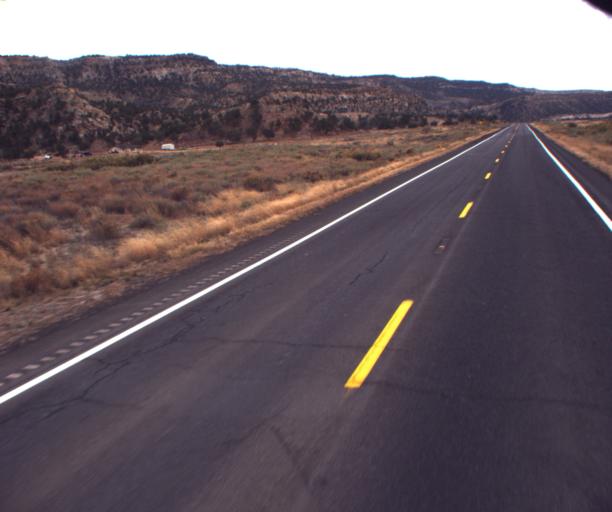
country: US
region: Arizona
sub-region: Navajo County
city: Kayenta
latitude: 36.5985
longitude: -110.4726
